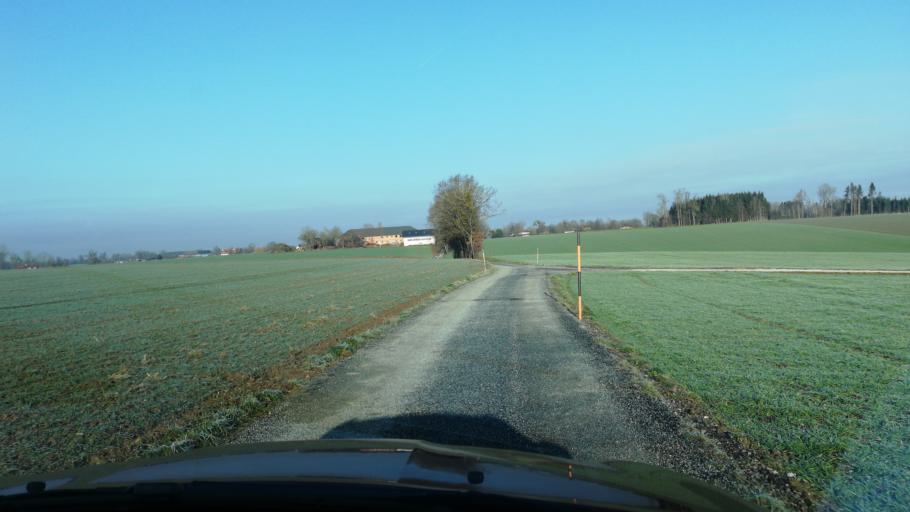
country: AT
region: Upper Austria
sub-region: Wels-Land
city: Thalheim bei Wels
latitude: 48.1367
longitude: 14.0387
